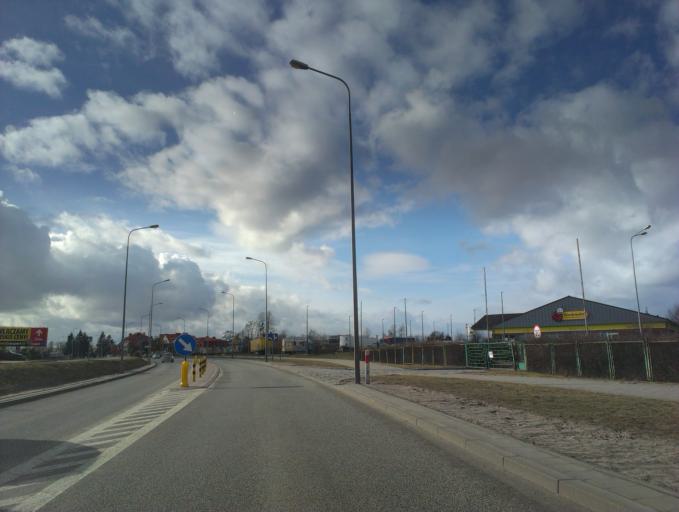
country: PL
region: Pomeranian Voivodeship
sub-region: Powiat czluchowski
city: Czluchow
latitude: 53.6734
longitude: 17.3626
